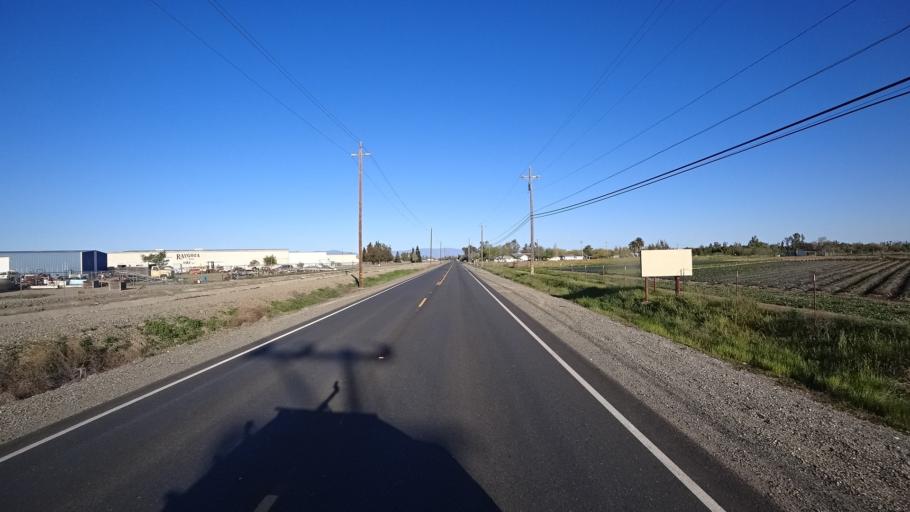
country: US
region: California
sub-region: Glenn County
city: Orland
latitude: 39.7559
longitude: -122.2184
